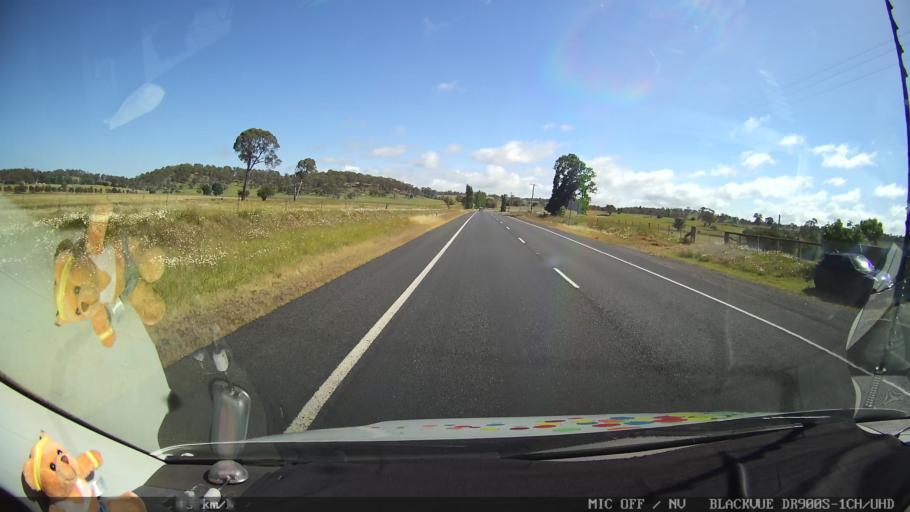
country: AU
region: New South Wales
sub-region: Guyra
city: Guyra
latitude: -30.1282
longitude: 151.6839
